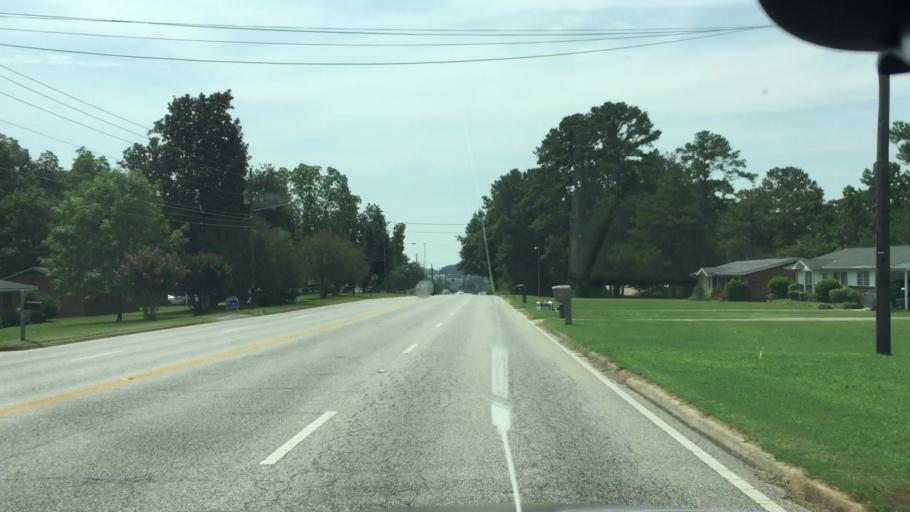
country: US
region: Alabama
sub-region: Coffee County
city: Enterprise
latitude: 31.3375
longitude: -85.8398
